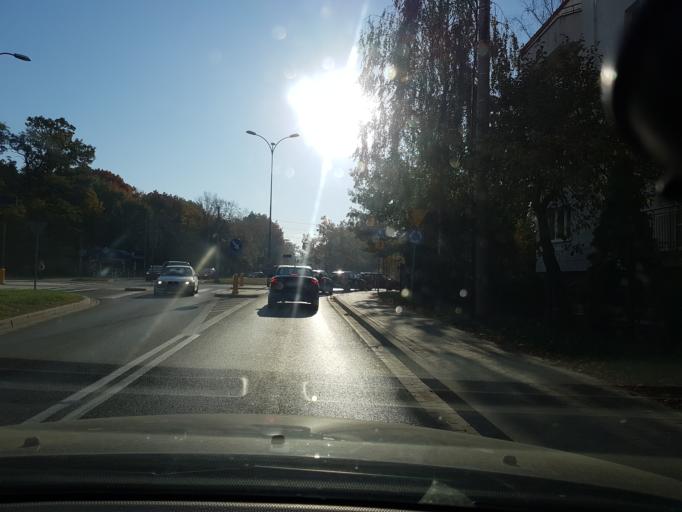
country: PL
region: Masovian Voivodeship
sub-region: Warszawa
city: Bemowo
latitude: 52.2595
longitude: 20.8970
